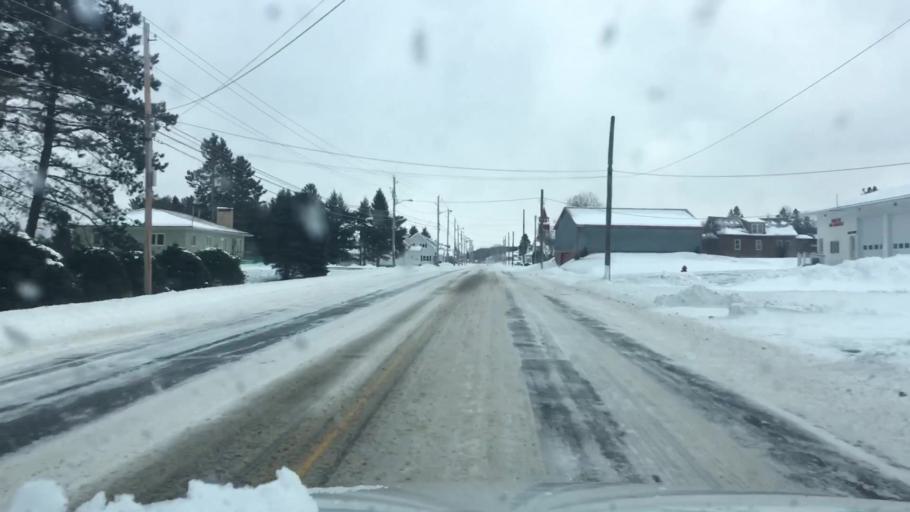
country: US
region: Maine
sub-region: Aroostook County
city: Madawaska
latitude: 47.3111
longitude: -68.1585
